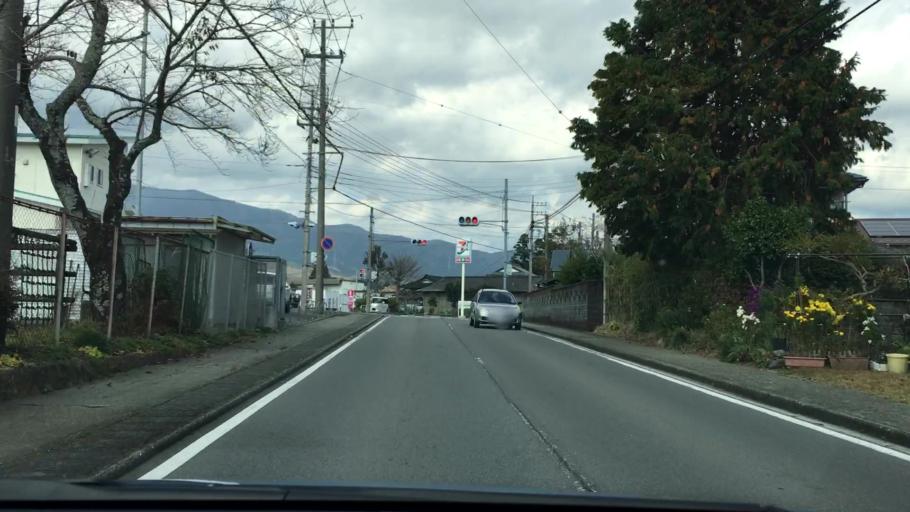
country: JP
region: Shizuoka
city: Gotemba
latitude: 35.3448
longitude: 138.9439
